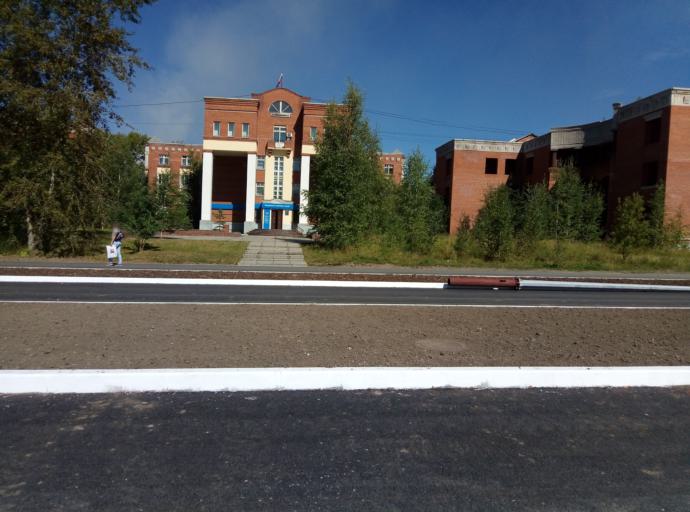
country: RU
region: Sverdlovsk
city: Krasnotur'insk
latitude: 59.7637
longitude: 60.1855
